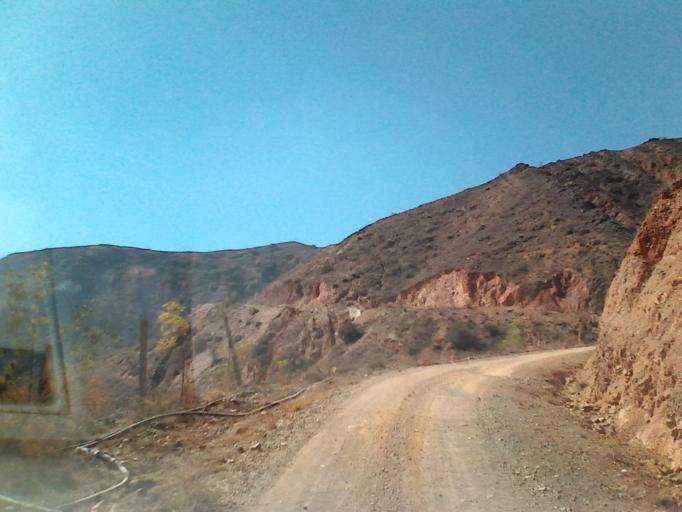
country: CO
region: Boyaca
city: Sachica
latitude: 5.5645
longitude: -73.5585
